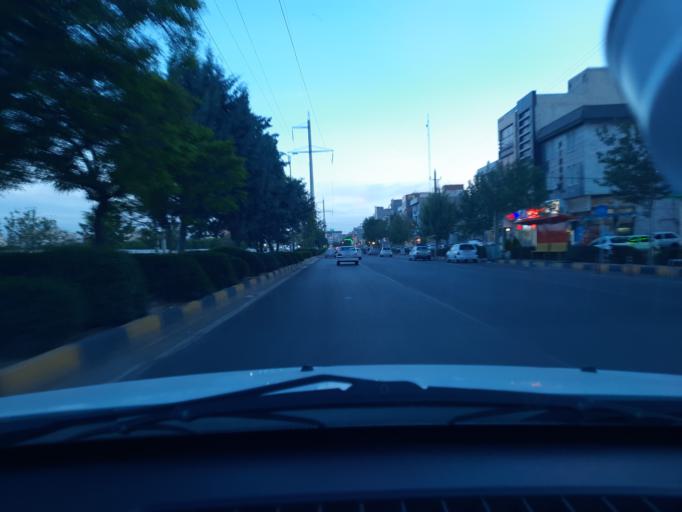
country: IR
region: Qazvin
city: Qazvin
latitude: 36.3044
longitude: 50.0110
